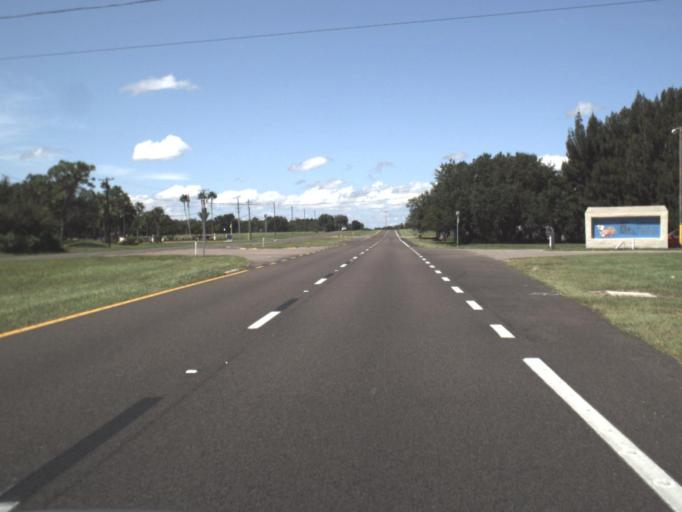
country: US
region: Florida
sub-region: Polk County
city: Lake Alfred
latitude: 28.1077
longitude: -81.6751
